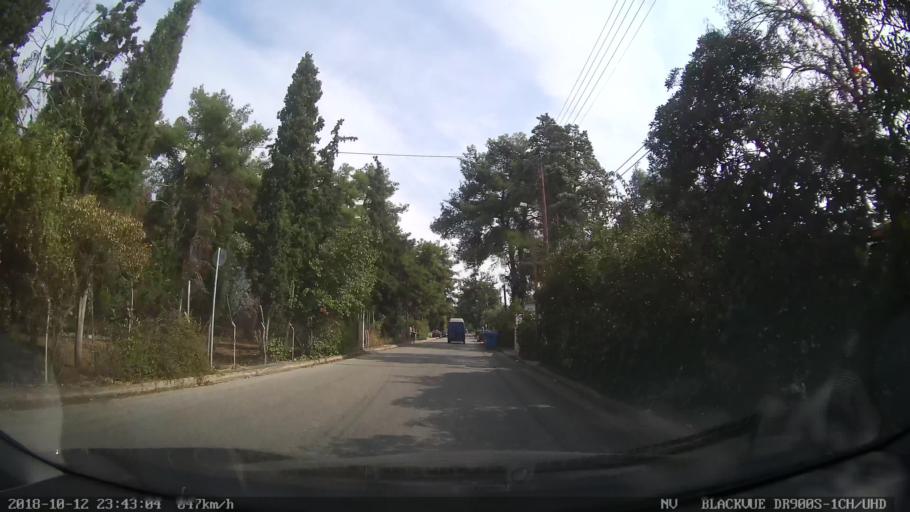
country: GR
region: Central Macedonia
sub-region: Nomos Thessalonikis
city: Pylaia
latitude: 40.5971
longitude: 22.9987
